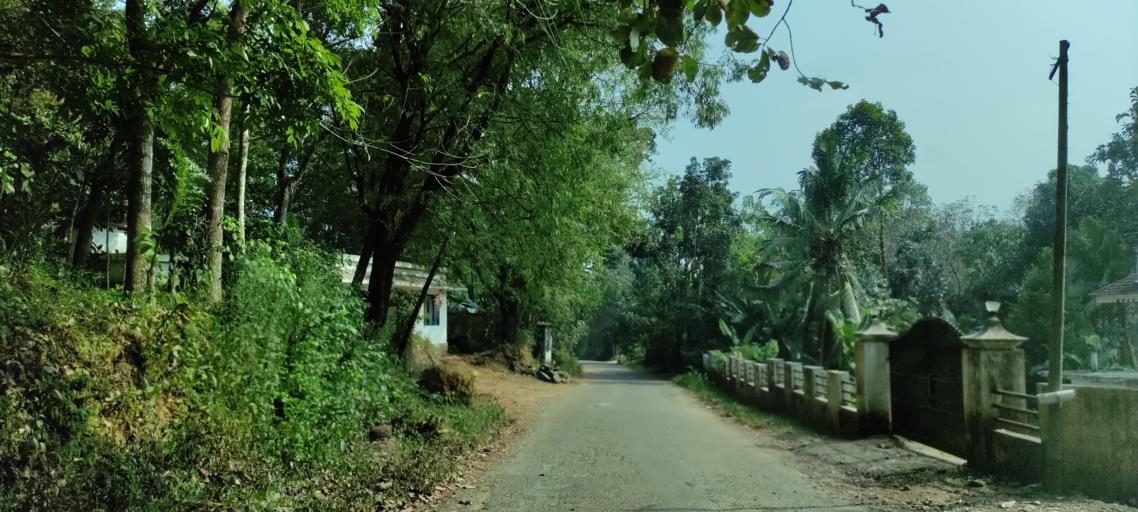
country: IN
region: Kerala
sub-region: Ernakulam
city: Piravam
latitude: 9.8218
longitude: 76.5129
